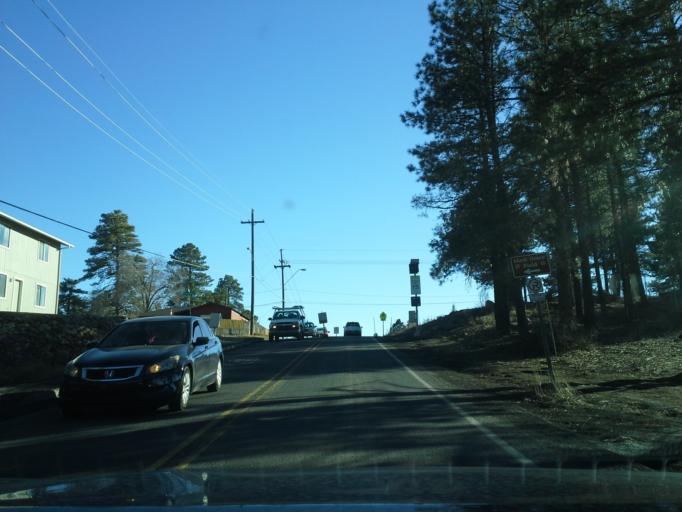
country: US
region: Arizona
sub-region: Coconino County
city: Flagstaff
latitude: 35.1821
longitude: -111.6482
